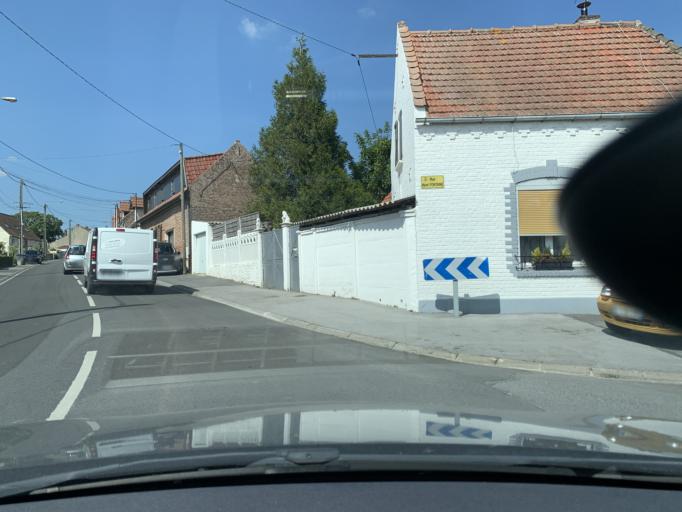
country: FR
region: Nord-Pas-de-Calais
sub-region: Departement du Pas-de-Calais
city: Oisy-le-Verger
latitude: 50.2490
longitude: 3.1184
